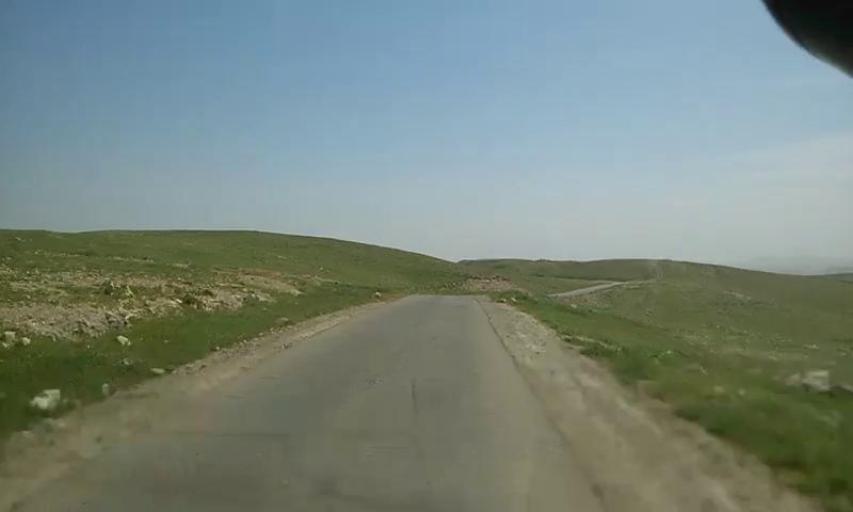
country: PS
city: `Arab ar Rashaydah
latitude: 31.5453
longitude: 35.2584
